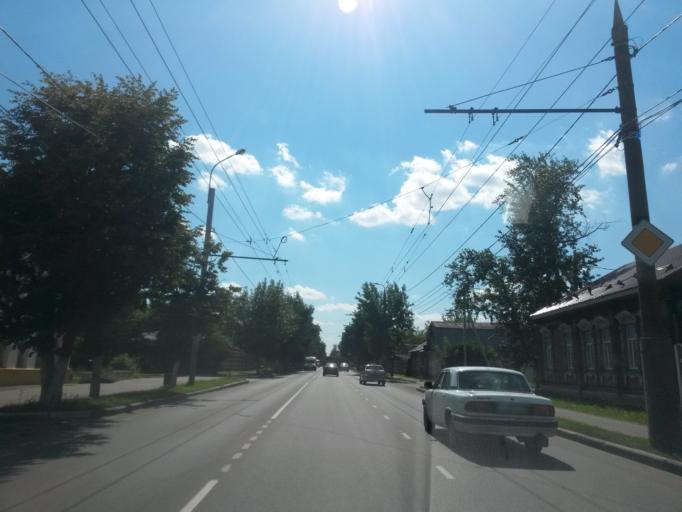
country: RU
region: Ivanovo
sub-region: Gorod Ivanovo
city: Ivanovo
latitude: 56.9907
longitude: 40.9850
